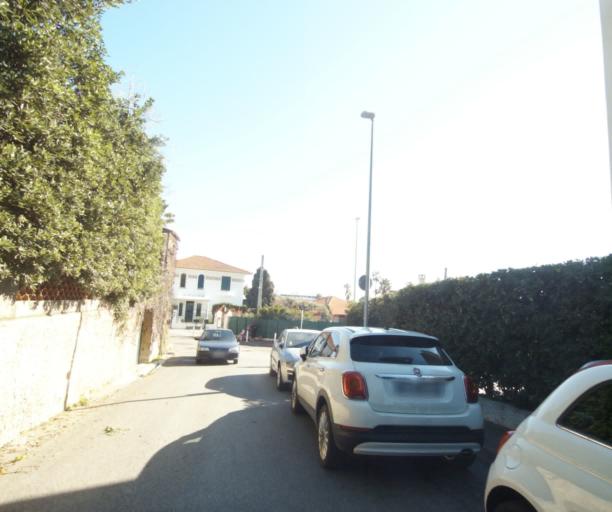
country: FR
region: Provence-Alpes-Cote d'Azur
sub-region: Departement des Alpes-Maritimes
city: Antibes
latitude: 43.5757
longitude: 7.1201
